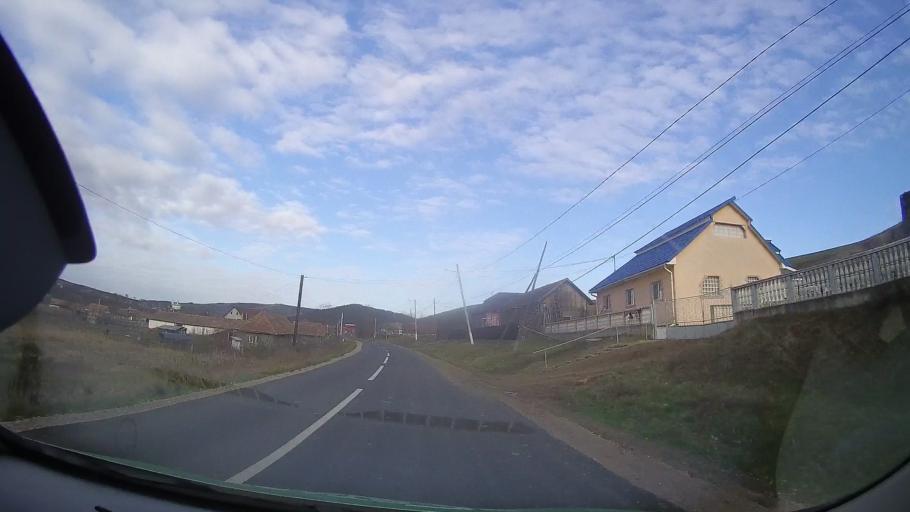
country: RO
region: Mures
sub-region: Comuna Iclanzel
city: Iclanzel
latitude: 46.5175
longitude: 24.2741
